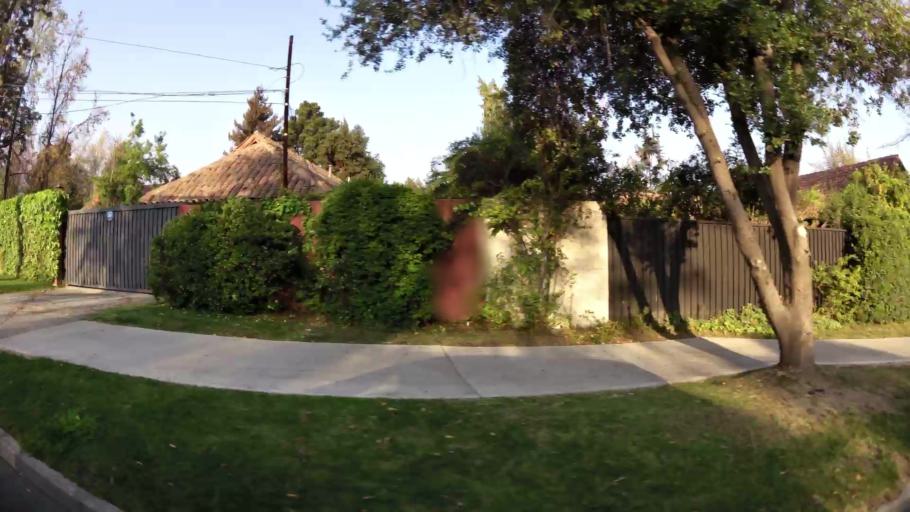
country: CL
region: Santiago Metropolitan
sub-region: Provincia de Santiago
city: Villa Presidente Frei, Nunoa, Santiago, Chile
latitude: -33.3478
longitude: -70.5104
